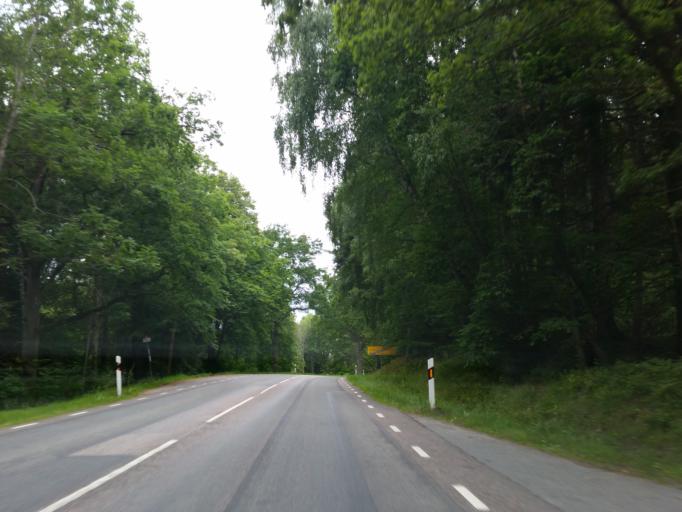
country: SE
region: Stockholm
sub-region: Sodertalje Kommun
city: Soedertaelje
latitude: 59.2020
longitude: 17.5579
